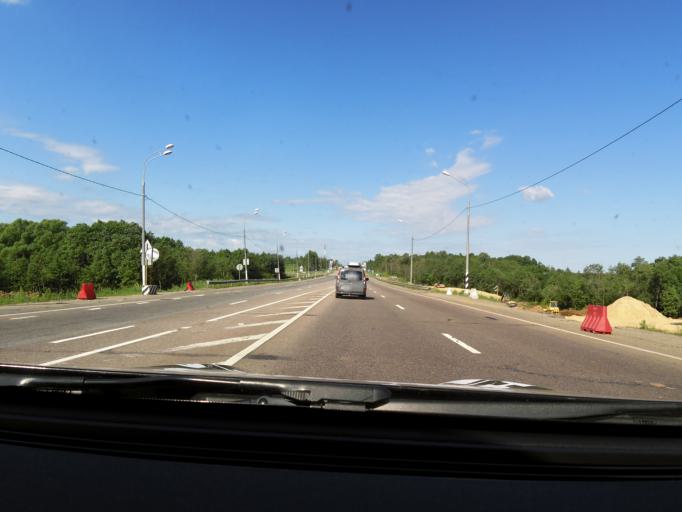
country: RU
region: Tverskaya
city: Emmaus
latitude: 56.7834
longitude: 36.0330
